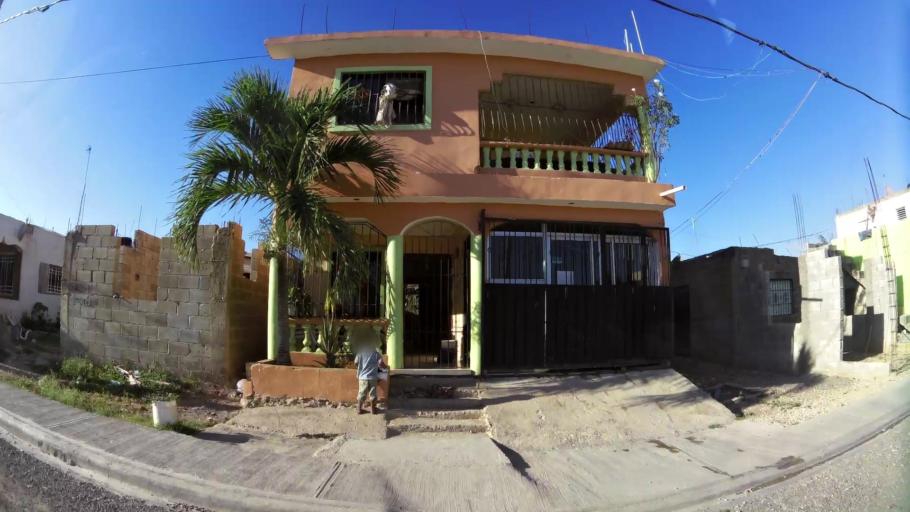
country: DO
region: Santo Domingo
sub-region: Santo Domingo
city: Santo Domingo Este
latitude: 18.4788
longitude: -69.8195
